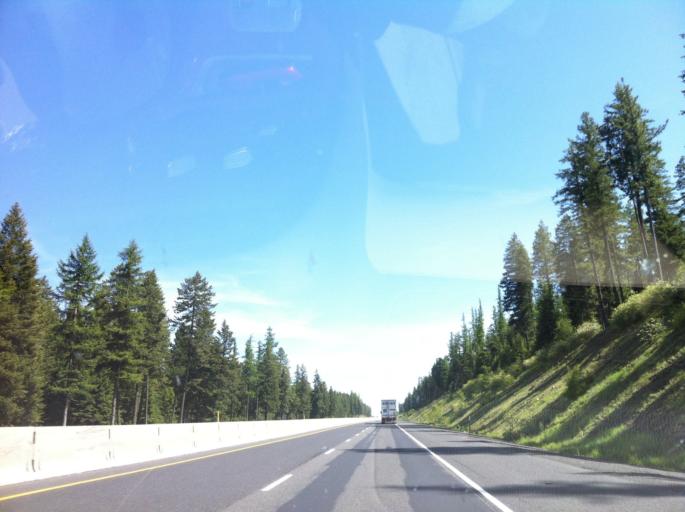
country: US
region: Oregon
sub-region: Umatilla County
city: Mission
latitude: 45.4932
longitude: -118.4141
